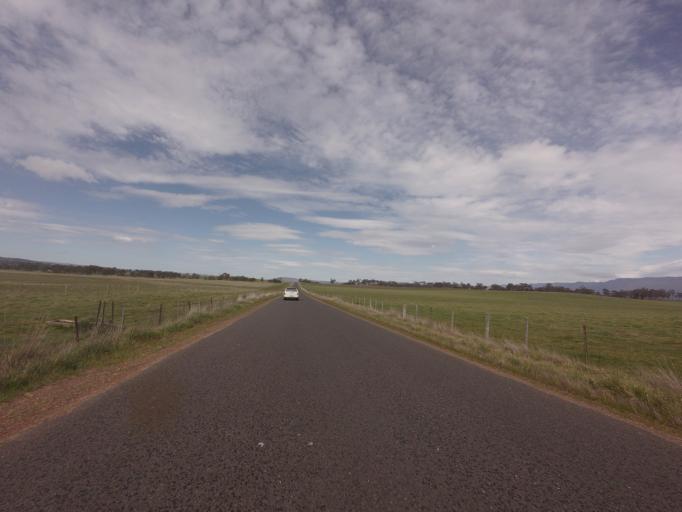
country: AU
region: Tasmania
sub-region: Northern Midlands
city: Evandale
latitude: -41.7930
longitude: 147.2505
